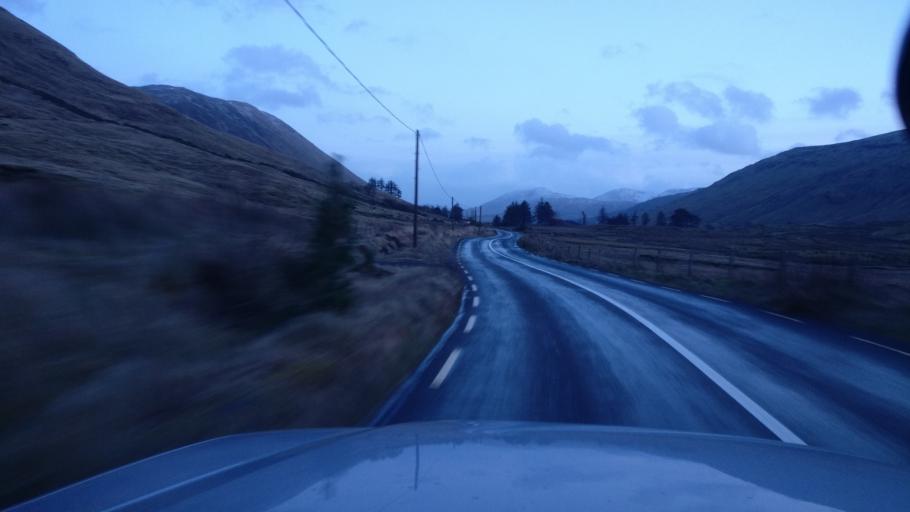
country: IE
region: Connaught
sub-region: Maigh Eo
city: Westport
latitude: 53.5802
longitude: -9.6693
